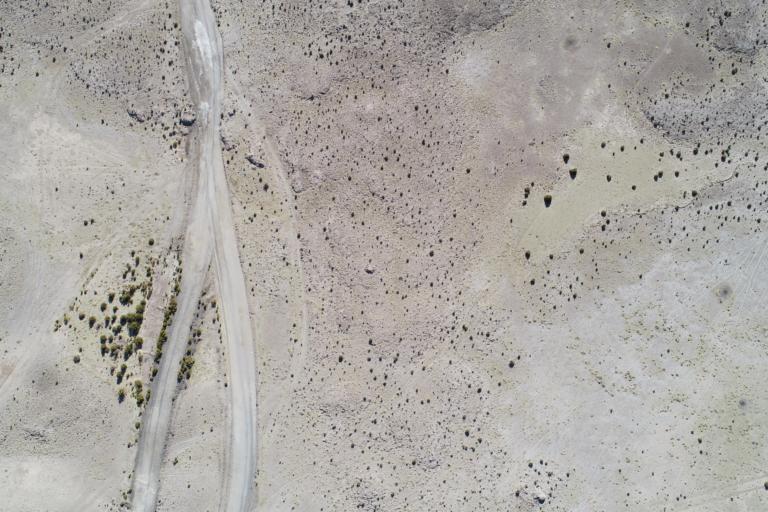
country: BO
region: Potosi
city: Colchani
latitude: -20.3520
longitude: -66.8924
